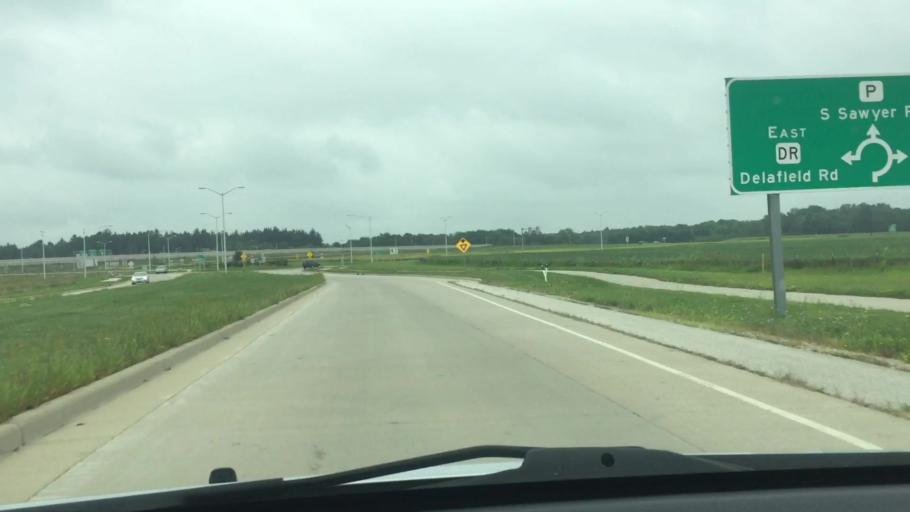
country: US
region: Wisconsin
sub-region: Waukesha County
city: Delafield
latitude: 43.0661
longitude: -88.4427
